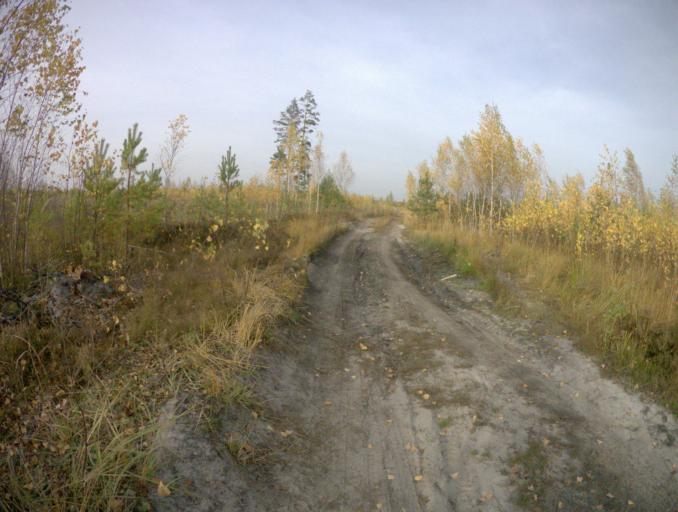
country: RU
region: Vladimir
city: Sobinka
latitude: 55.9796
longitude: 40.0662
